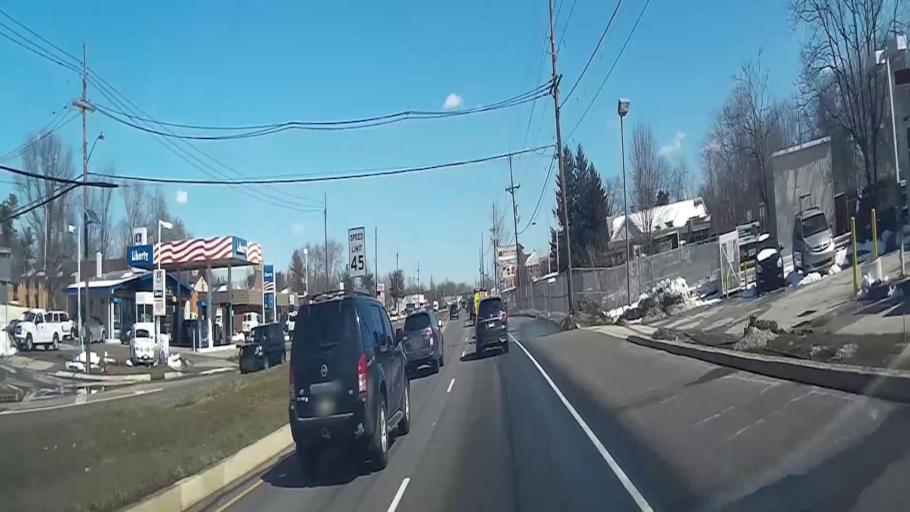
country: US
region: New Jersey
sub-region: Camden County
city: Greentree
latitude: 39.8957
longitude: -74.9447
